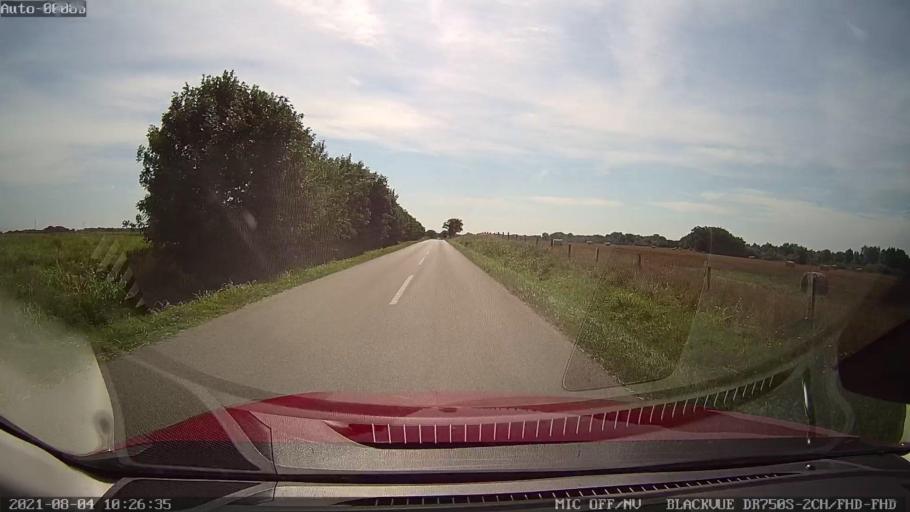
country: HR
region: Osjecko-Baranjska
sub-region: Grad Osijek
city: Bilje
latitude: 45.6060
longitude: 18.7659
